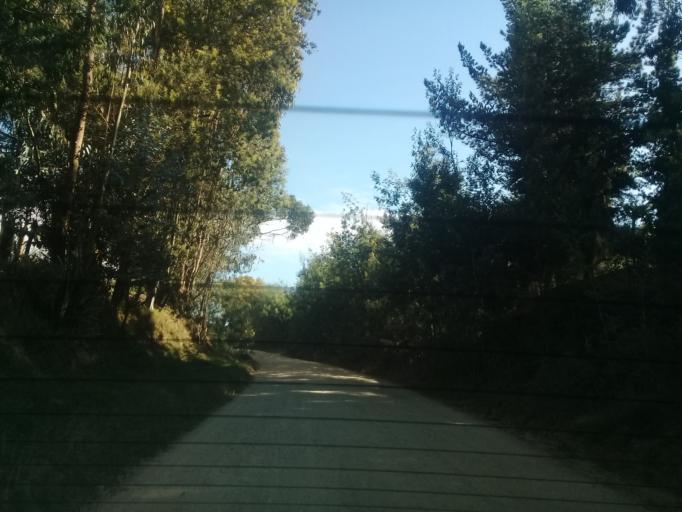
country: CO
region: Cundinamarca
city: Tocancipa
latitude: 4.9275
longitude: -73.8818
